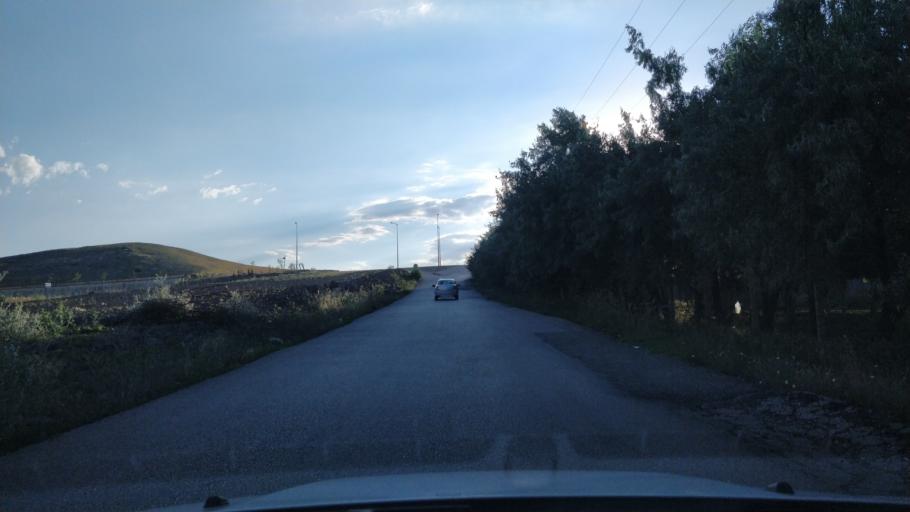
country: TR
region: Ankara
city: Etimesgut
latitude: 39.8272
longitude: 32.5576
